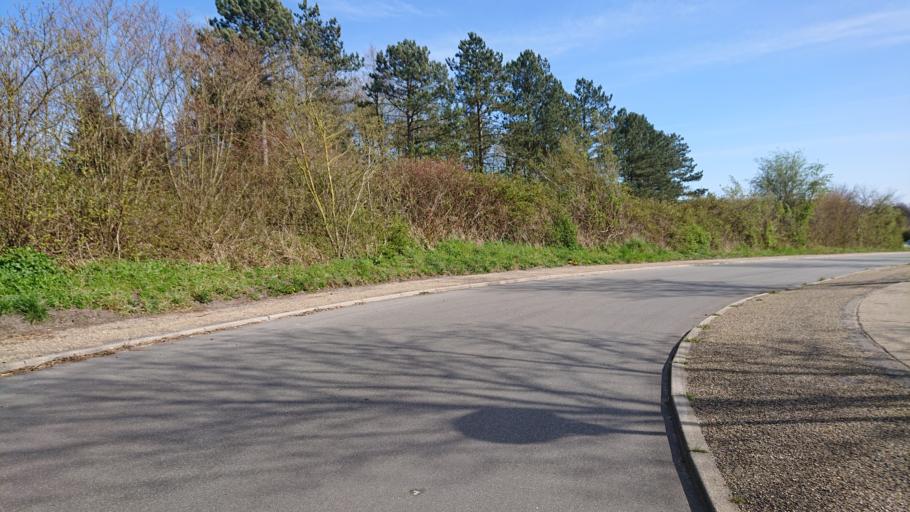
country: DK
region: South Denmark
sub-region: Nyborg Kommune
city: Nyborg
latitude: 55.3039
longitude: 10.7693
